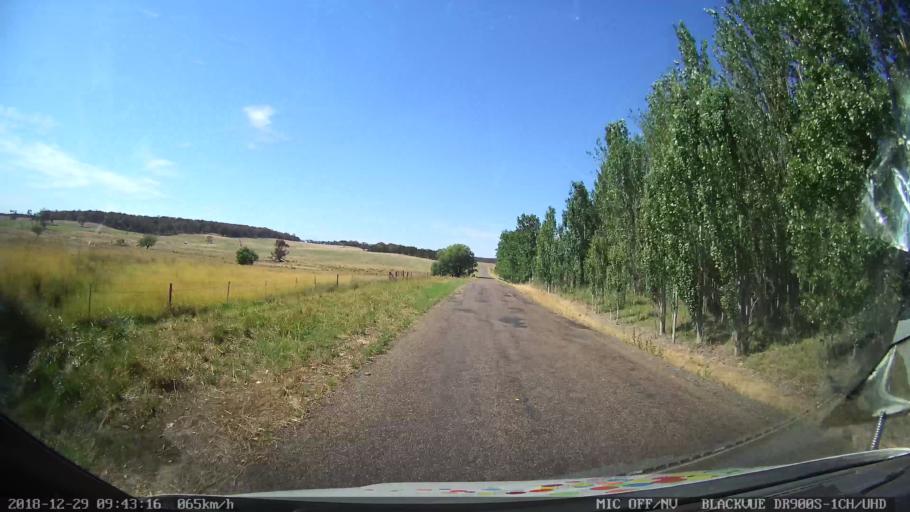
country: AU
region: New South Wales
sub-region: Upper Lachlan Shire
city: Crookwell
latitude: -34.6775
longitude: 149.4246
